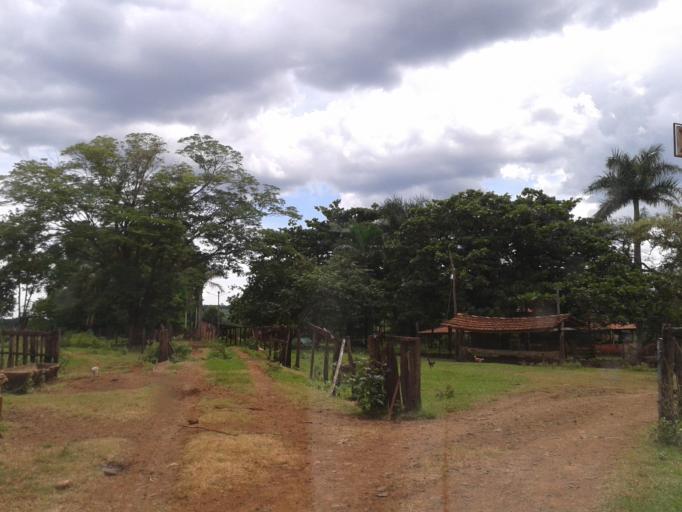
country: BR
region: Minas Gerais
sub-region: Centralina
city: Centralina
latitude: -18.6677
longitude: -49.2370
